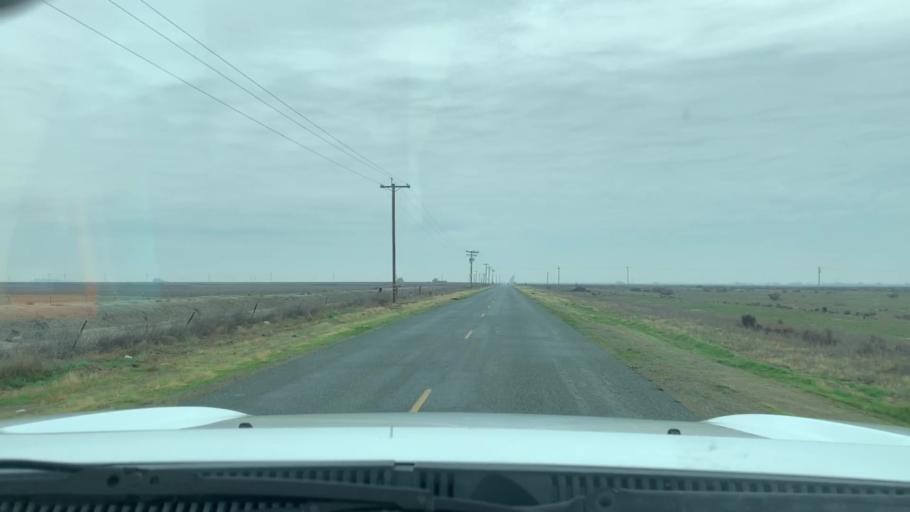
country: US
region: California
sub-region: Tulare County
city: Alpaugh
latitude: 35.7610
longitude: -119.4820
